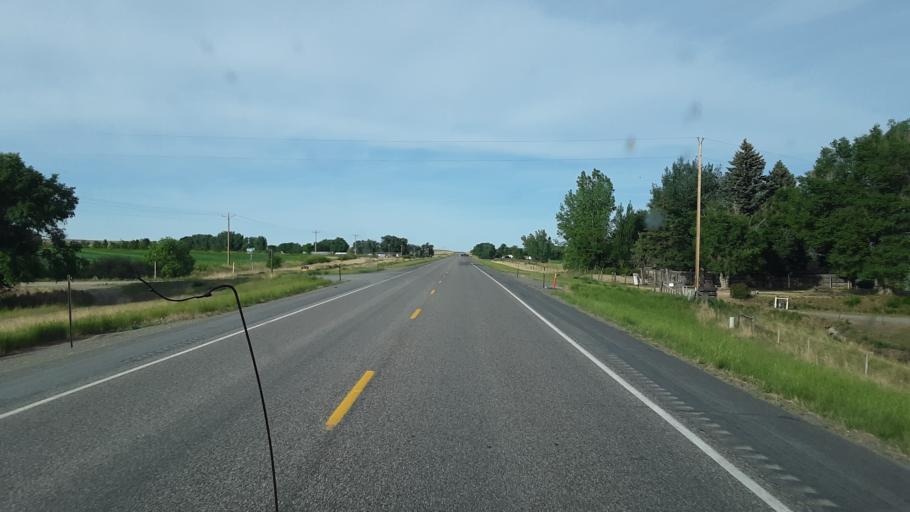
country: US
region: Wyoming
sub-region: Fremont County
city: Riverton
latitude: 43.1764
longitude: -108.2545
